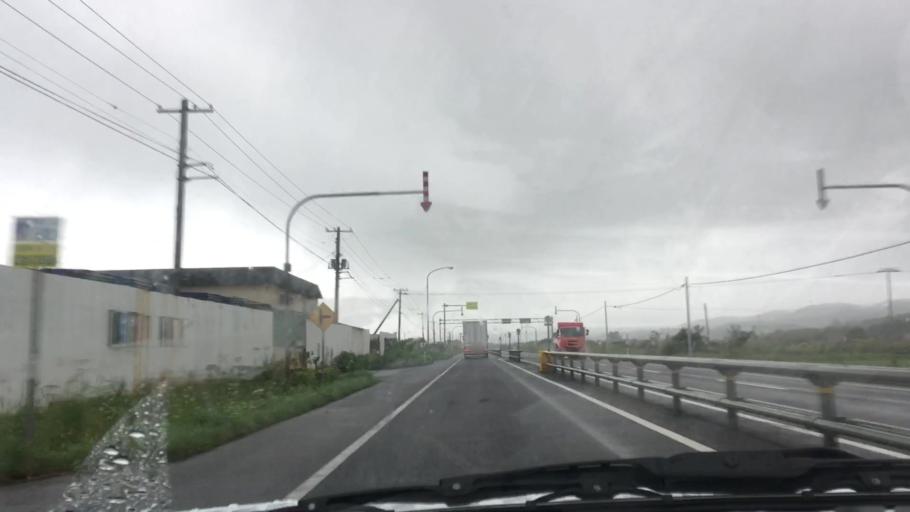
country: JP
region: Hokkaido
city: Niseko Town
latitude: 42.4145
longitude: 140.3092
